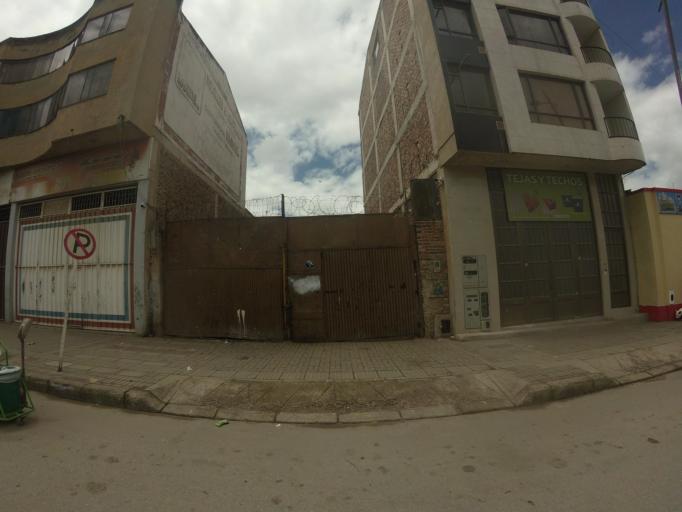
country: CO
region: Boyaca
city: Duitama
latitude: 5.8228
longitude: -73.0323
